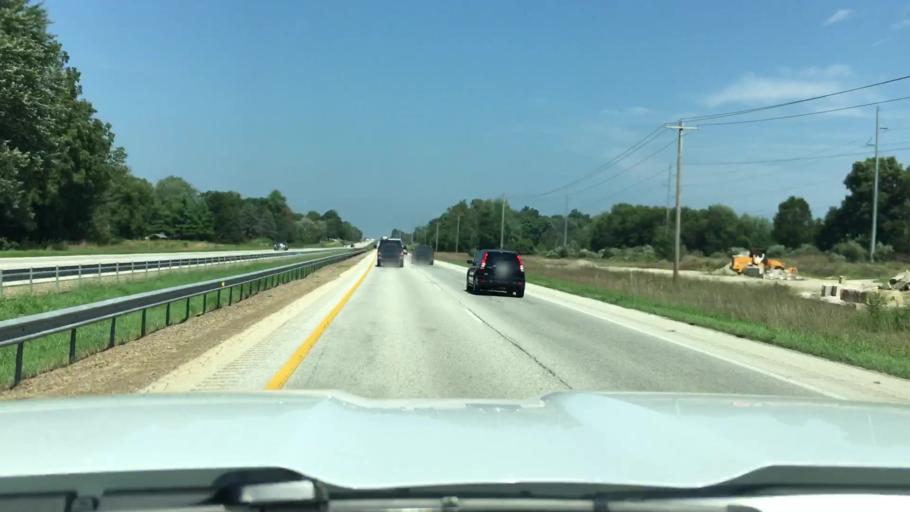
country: US
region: Michigan
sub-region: Kalamazoo County
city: Schoolcraft
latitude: 42.0516
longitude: -85.6356
